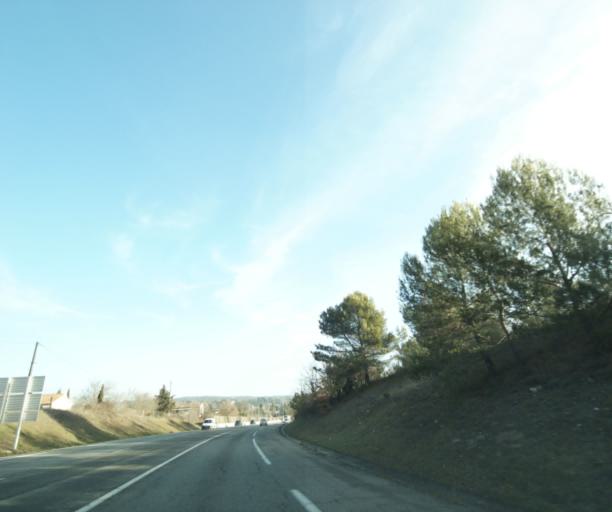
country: FR
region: Provence-Alpes-Cote d'Azur
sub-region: Departement du Var
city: Saint-Maximin-la-Sainte-Baume
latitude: 43.4459
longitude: 5.8721
